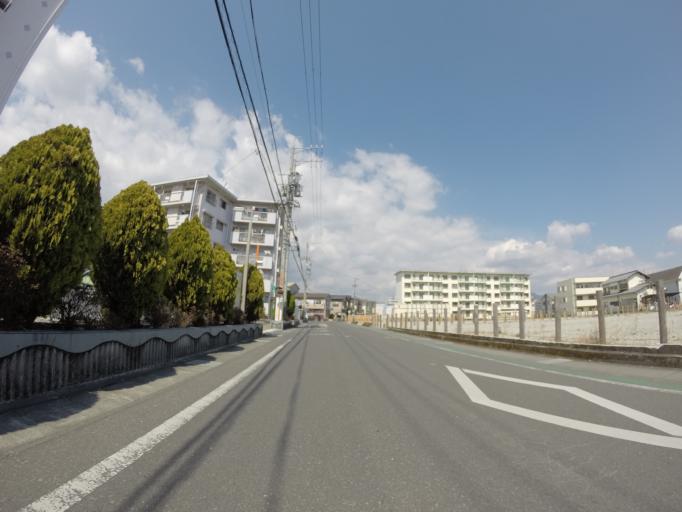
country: JP
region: Shizuoka
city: Shizuoka-shi
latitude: 34.9895
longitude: 138.3643
